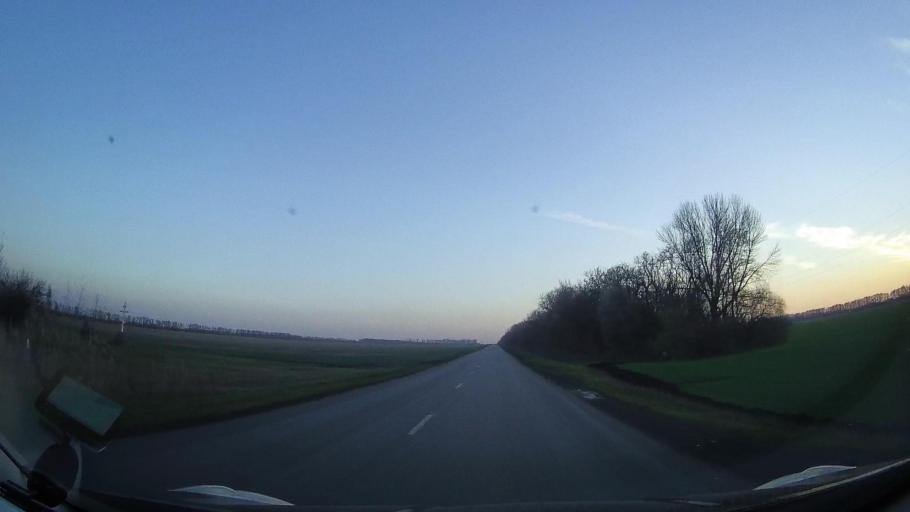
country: RU
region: Rostov
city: Zernograd
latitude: 47.0416
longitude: 40.3916
